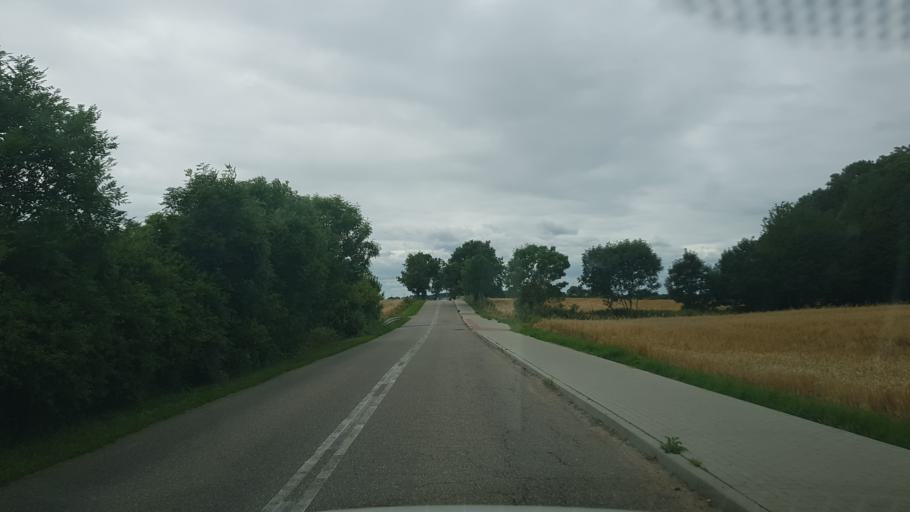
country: PL
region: West Pomeranian Voivodeship
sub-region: Powiat gryficki
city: Cerkwica
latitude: 54.0858
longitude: 15.1166
